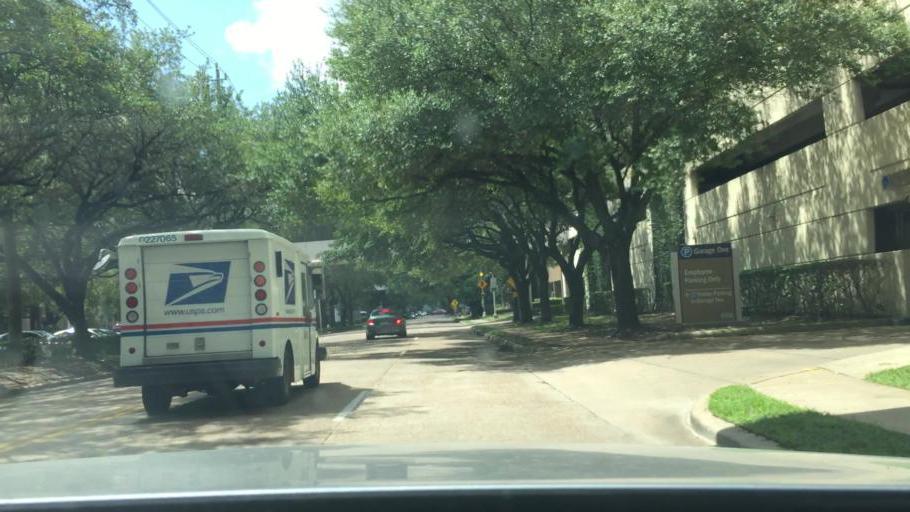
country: US
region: Texas
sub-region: Harris County
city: Bunker Hill Village
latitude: 29.7821
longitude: -95.5478
